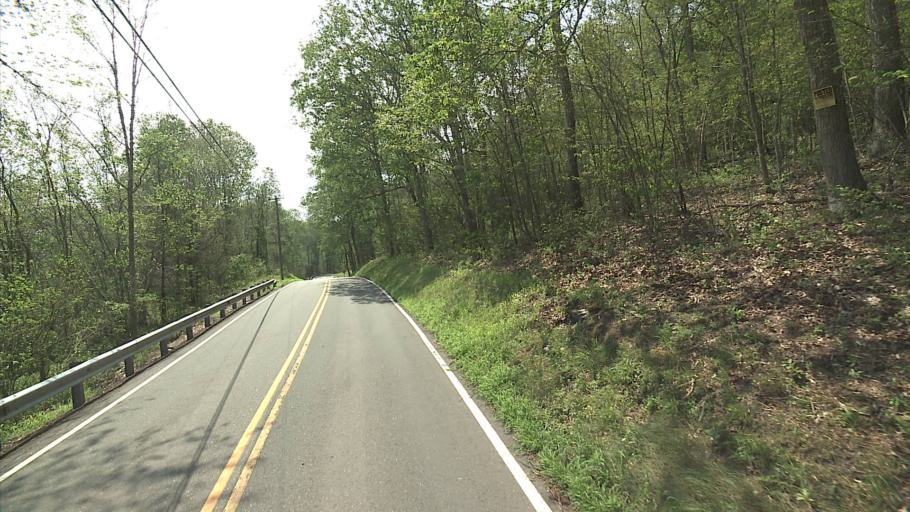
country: US
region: Connecticut
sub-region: Windham County
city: Moosup
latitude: 41.7530
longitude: -71.8532
